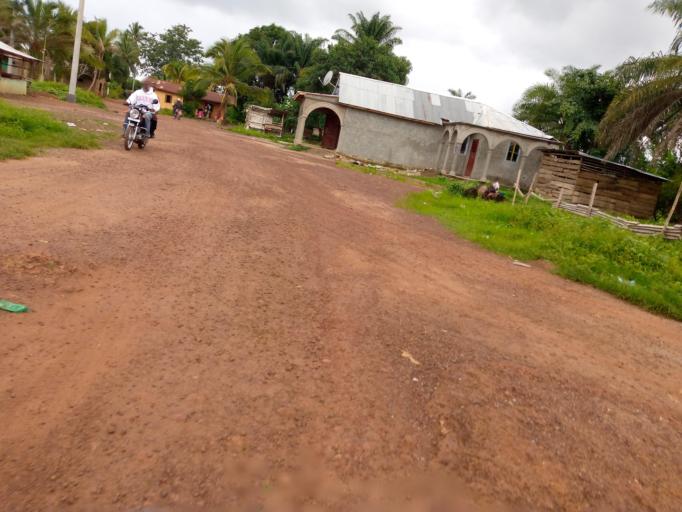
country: SL
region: Southern Province
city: Moyamba
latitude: 8.1521
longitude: -12.4346
